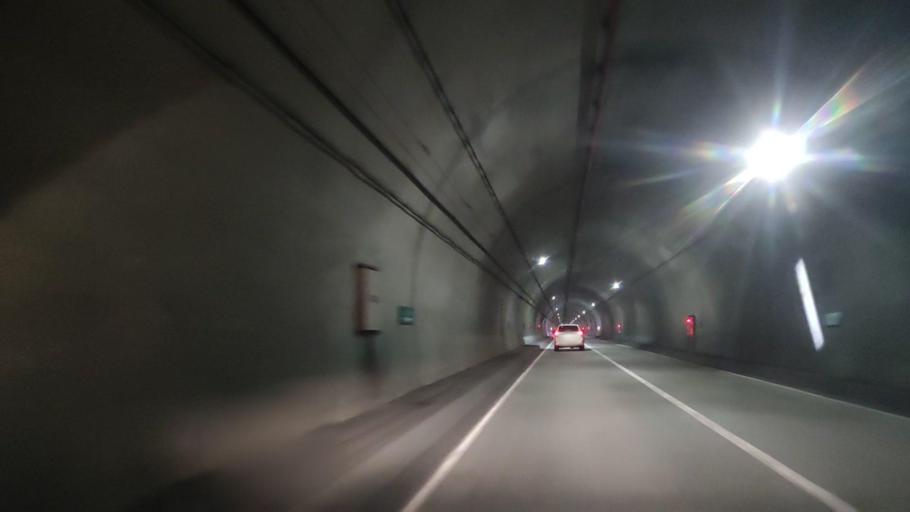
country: JP
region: Hokkaido
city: Rumoi
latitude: 43.7162
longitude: 141.3296
